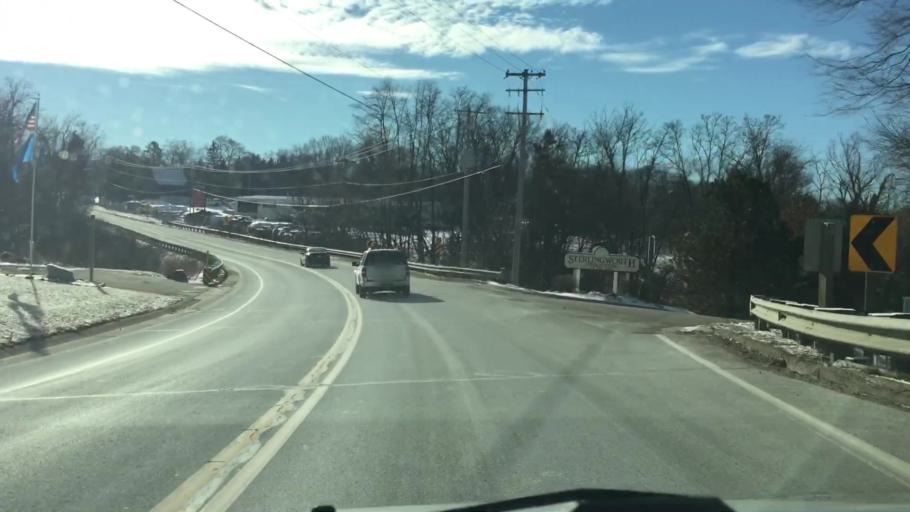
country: US
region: Wisconsin
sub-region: Walworth County
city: Elkhorn
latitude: 42.7671
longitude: -88.5558
